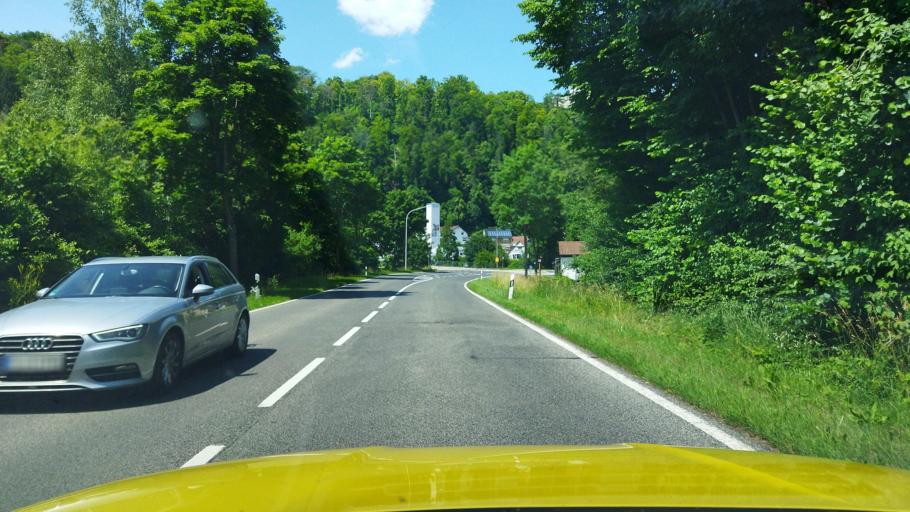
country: DE
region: Bavaria
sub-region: Lower Bavaria
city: Riedenburg
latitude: 48.9566
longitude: 11.6819
